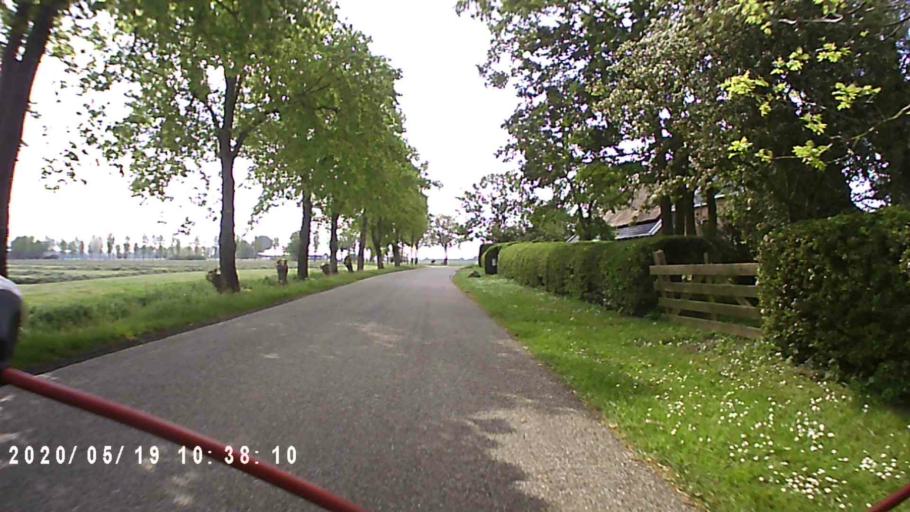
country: NL
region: Friesland
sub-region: Gemeente Kollumerland en Nieuwkruisland
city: Kollum
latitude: 53.2727
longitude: 6.1873
